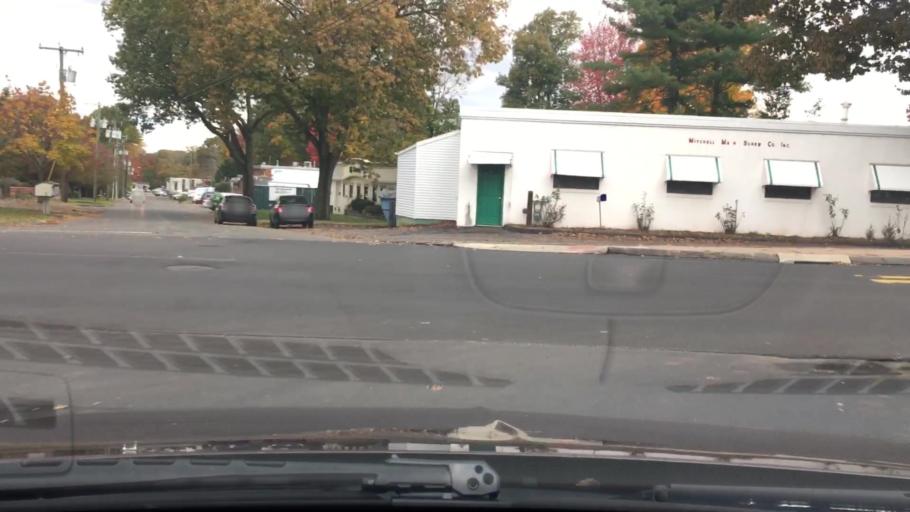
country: US
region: Connecticut
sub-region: Hartford County
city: Glastonbury Center
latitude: 41.7106
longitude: -72.5916
